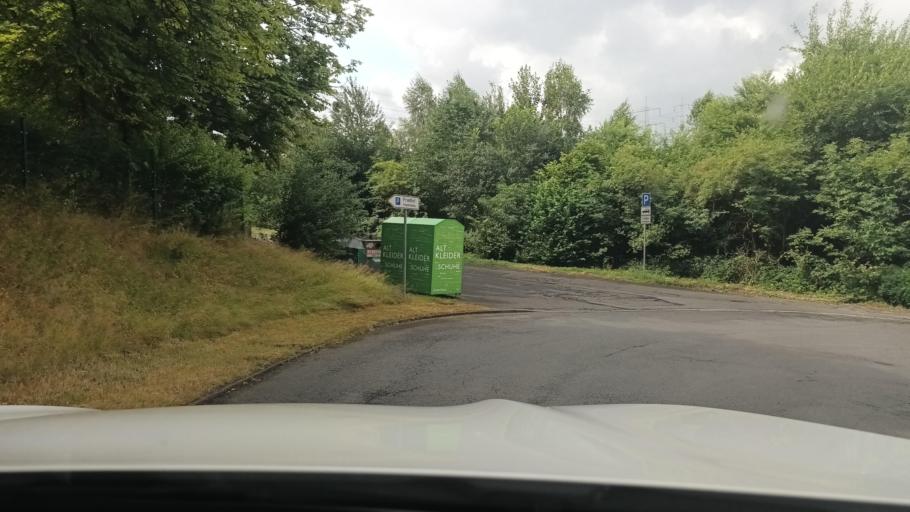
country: DE
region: North Rhine-Westphalia
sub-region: Regierungsbezirk Koln
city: Eitorf
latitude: 50.7587
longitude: 7.4469
